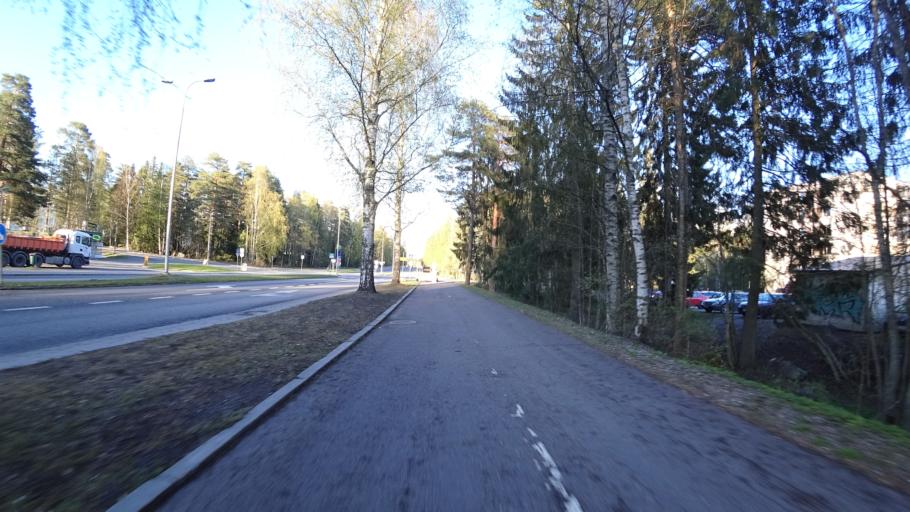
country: FI
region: Pirkanmaa
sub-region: Tampere
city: Pirkkala
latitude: 61.5045
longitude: 23.6169
